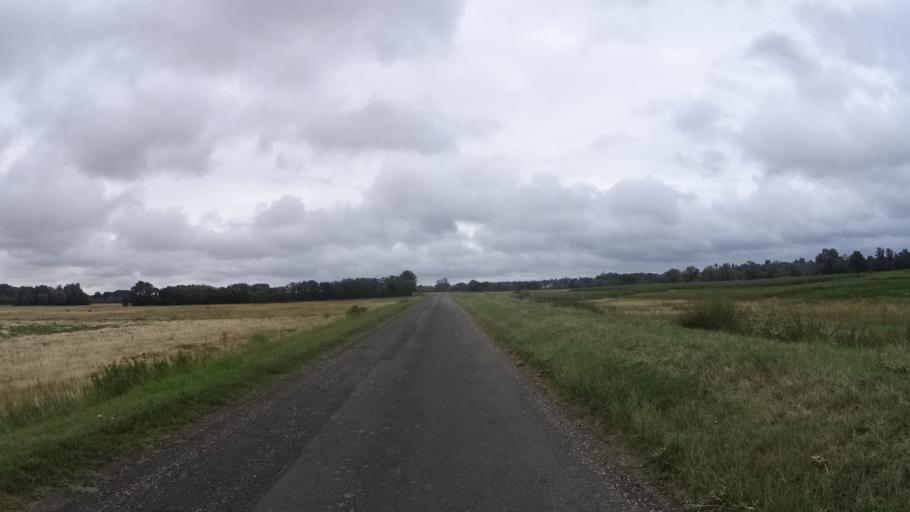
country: FR
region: Centre
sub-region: Departement du Loir-et-Cher
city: Suevres
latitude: 47.6581
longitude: 1.4677
